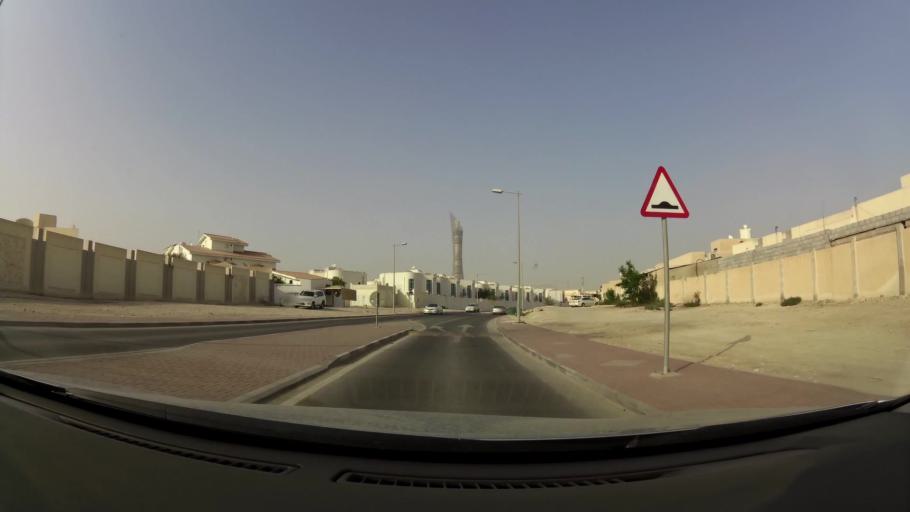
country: QA
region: Baladiyat ar Rayyan
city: Ar Rayyan
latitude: 25.2521
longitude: 51.4383
